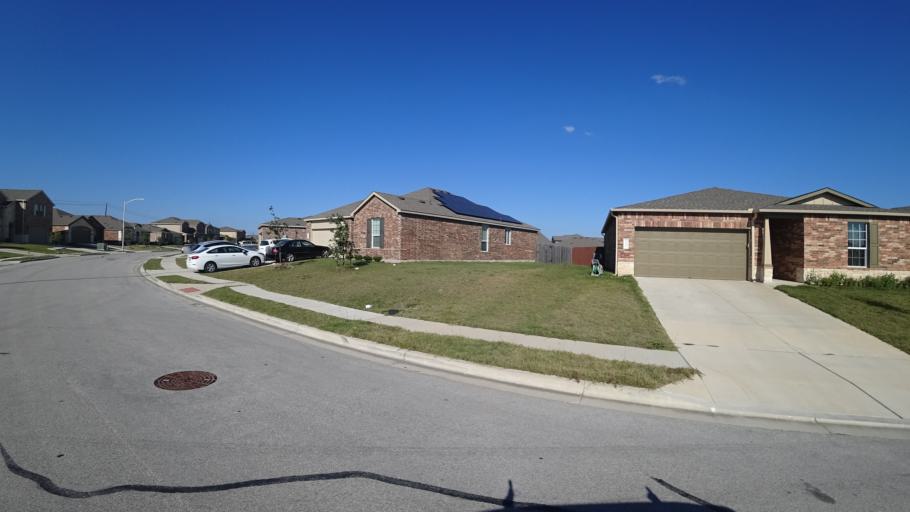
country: US
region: Texas
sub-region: Travis County
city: Manor
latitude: 30.3557
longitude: -97.6219
